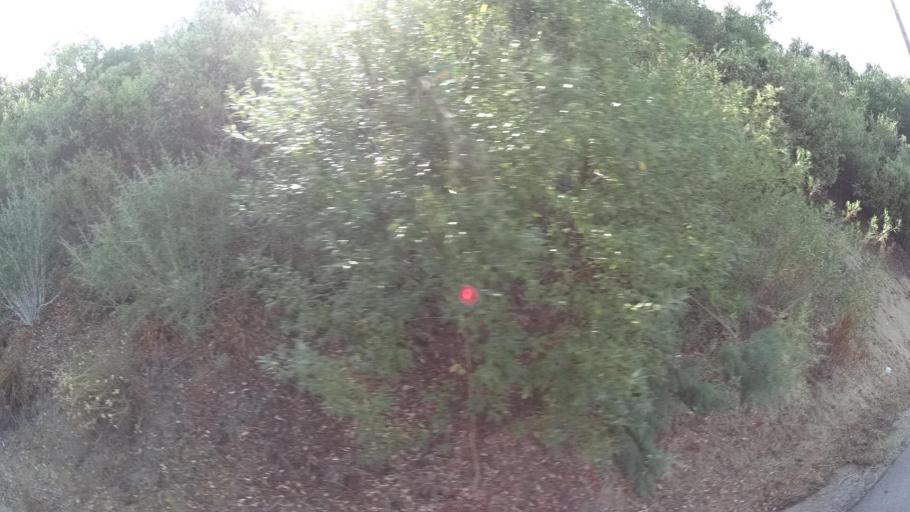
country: US
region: California
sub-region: San Diego County
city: Julian
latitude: 33.0999
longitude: -116.6581
